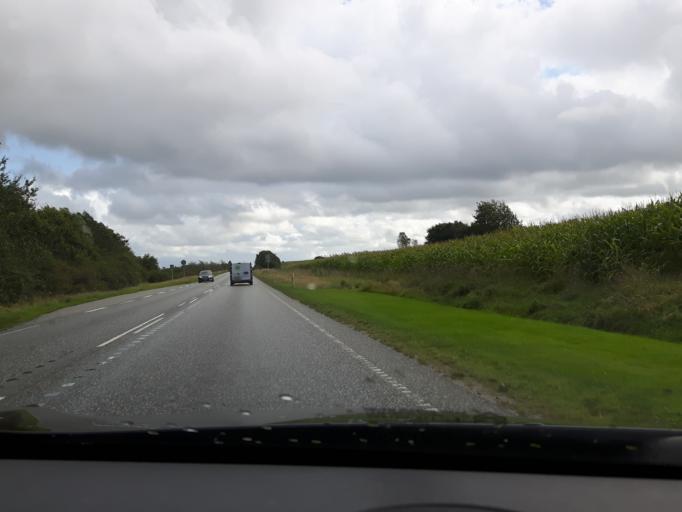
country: DK
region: Central Jutland
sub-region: Herning Kommune
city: Avlum
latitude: 56.2809
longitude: 8.7518
